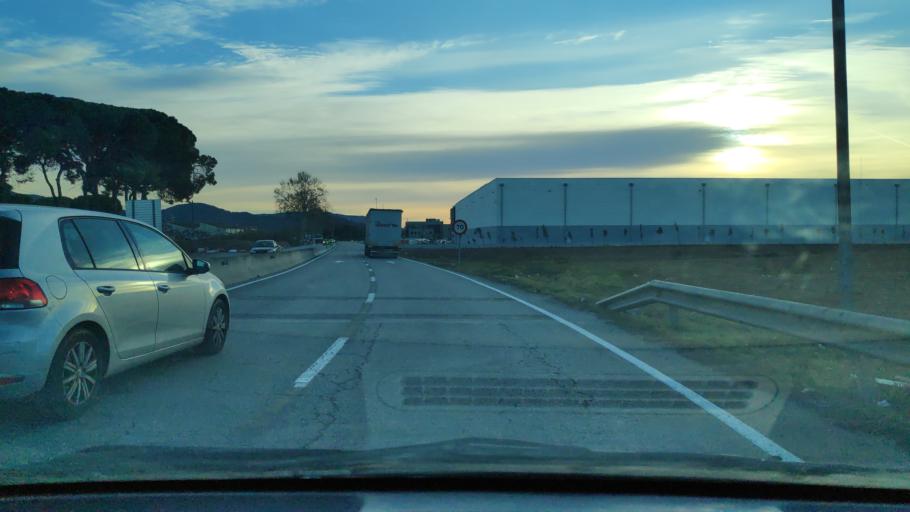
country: ES
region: Catalonia
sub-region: Provincia de Barcelona
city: Llica de Vall
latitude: 41.5743
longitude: 2.2719
